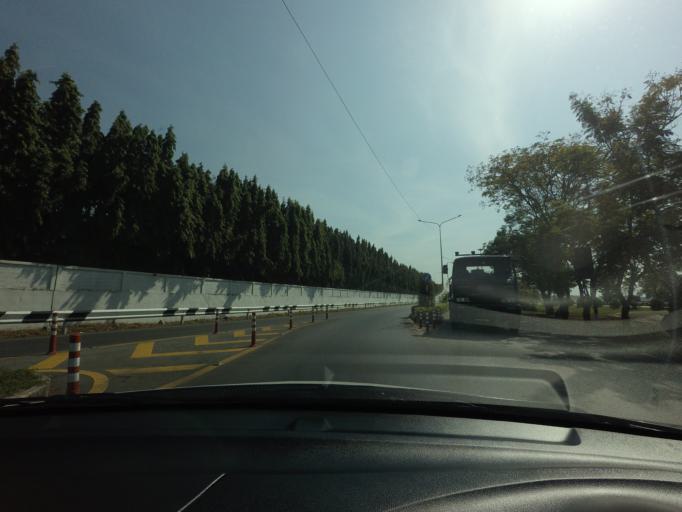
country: TH
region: Bangkok
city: Don Mueang
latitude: 13.9367
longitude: 100.6132
